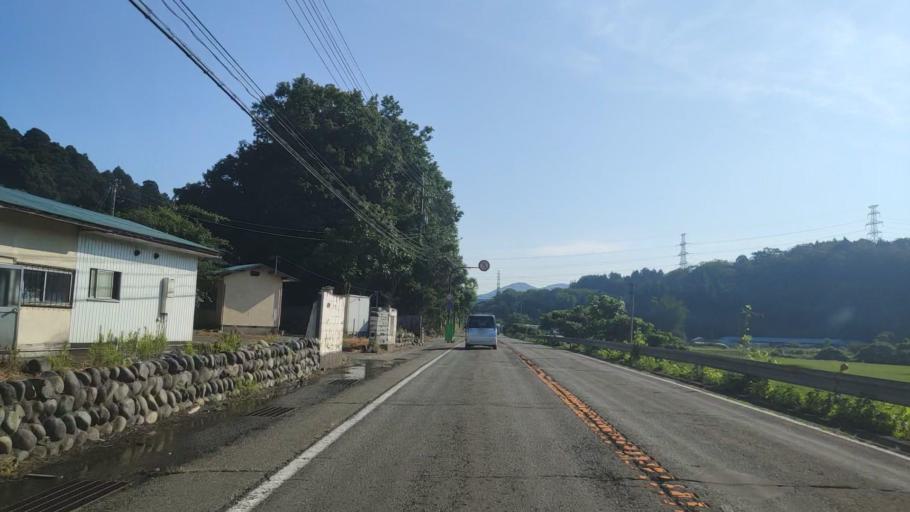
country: JP
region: Fukui
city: Maruoka
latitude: 36.2203
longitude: 136.2762
